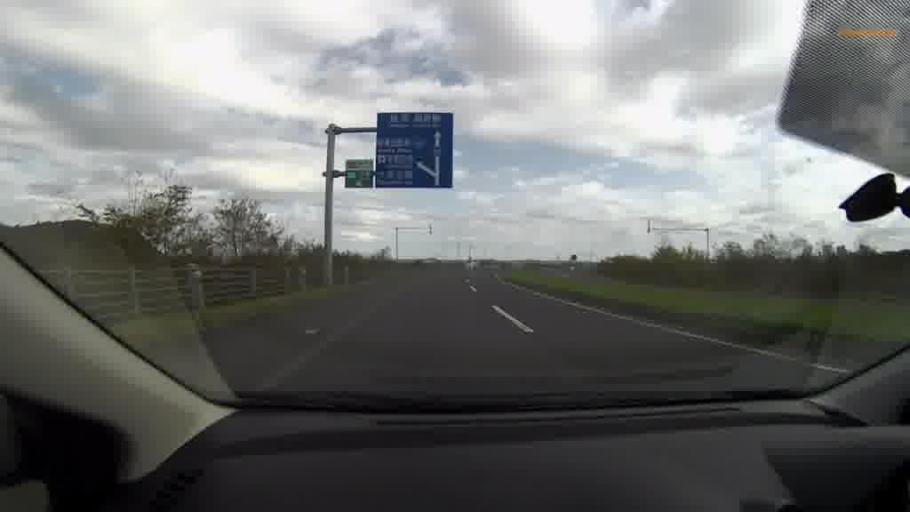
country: JP
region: Hokkaido
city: Kushiro
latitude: 43.0185
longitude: 144.2569
